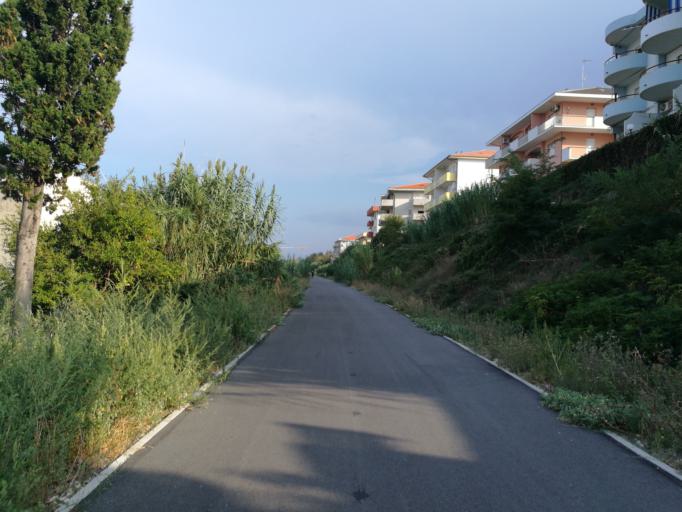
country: IT
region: Abruzzo
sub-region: Provincia di Chieti
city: Fossacesia
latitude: 42.2502
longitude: 14.5099
